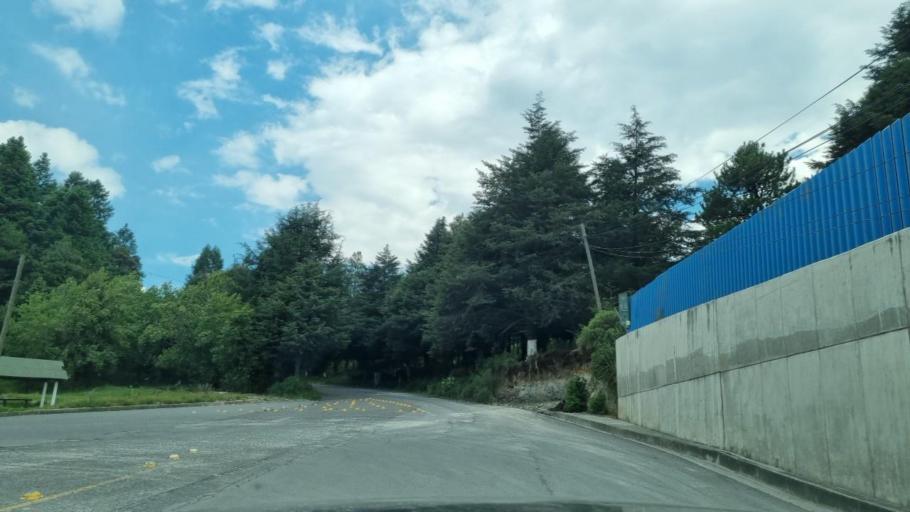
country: MX
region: Morelos
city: San Jeronimo Acazulco
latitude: 19.2973
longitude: -99.3926
